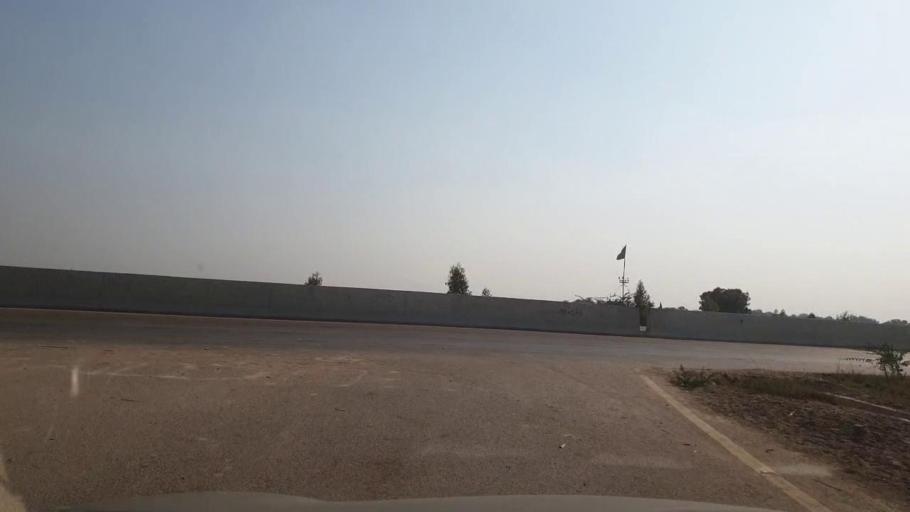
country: PK
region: Sindh
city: Tando Allahyar
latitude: 25.4927
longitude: 68.8660
